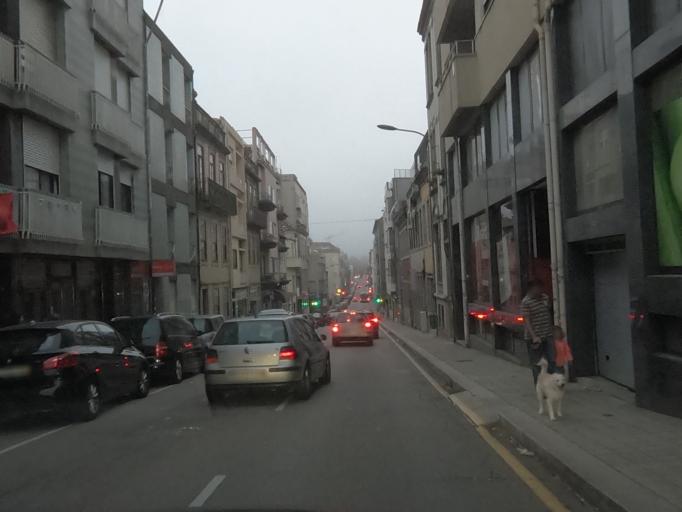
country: PT
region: Porto
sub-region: Porto
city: Porto
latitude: 41.1561
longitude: -8.6182
